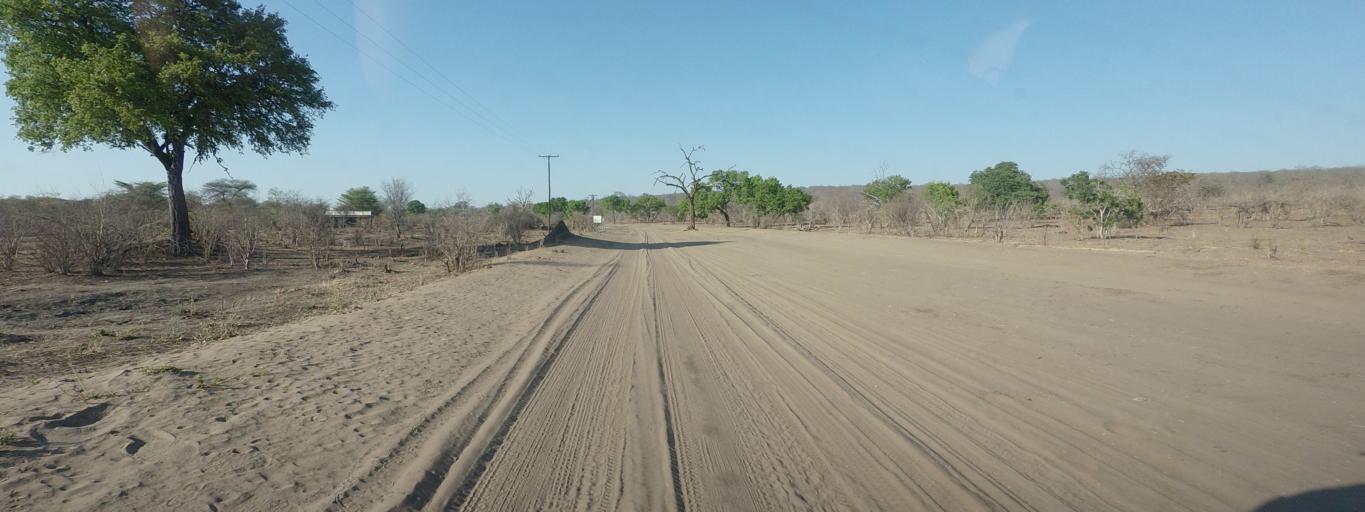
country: BW
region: North West
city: Kasane
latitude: -17.8857
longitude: 25.2306
